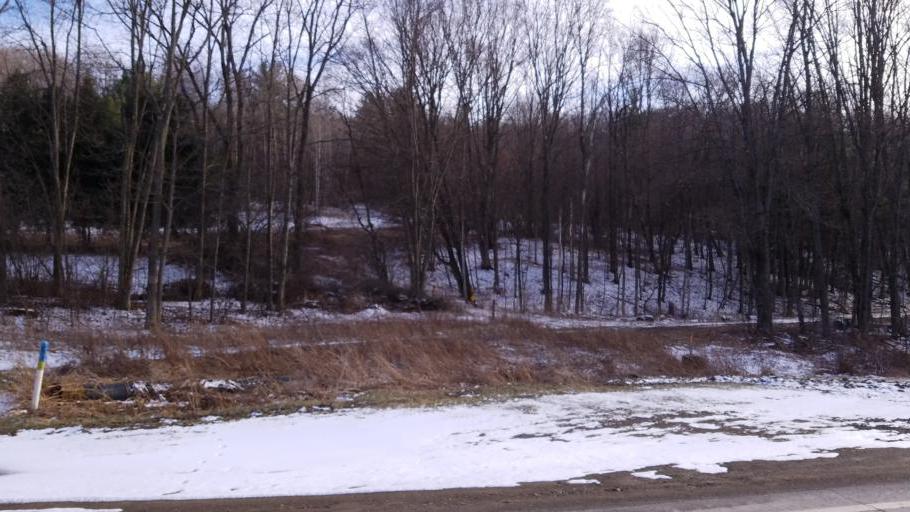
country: US
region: New York
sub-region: Allegany County
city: Wellsville
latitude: 42.1677
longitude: -77.9563
